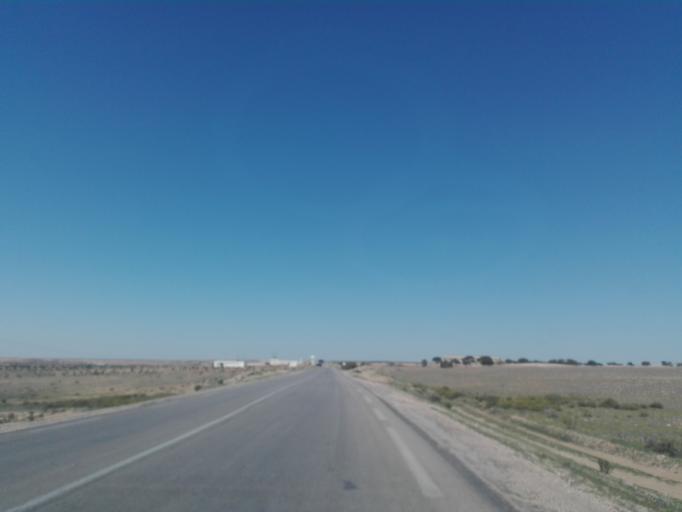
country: TN
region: Safaqis
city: Bi'r `Ali Bin Khalifah
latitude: 34.7384
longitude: 10.4058
